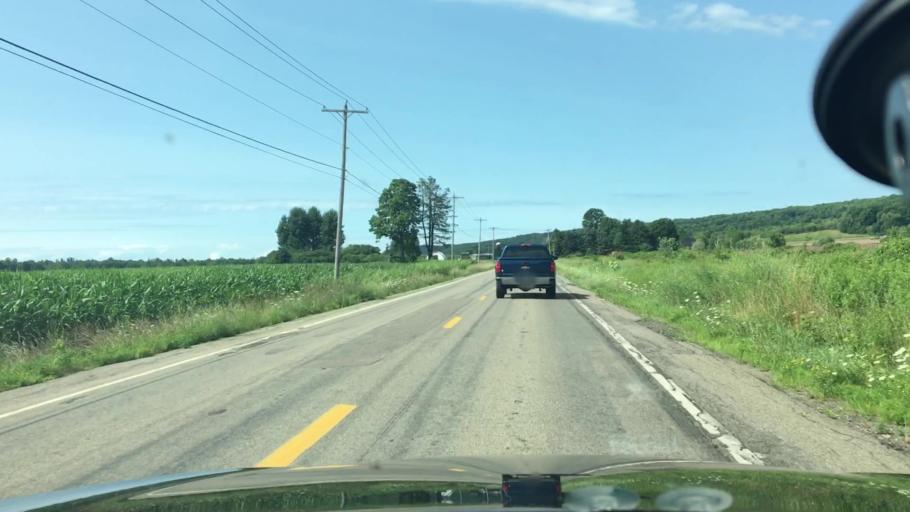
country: US
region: New York
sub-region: Chautauqua County
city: Brocton
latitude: 42.2962
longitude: -79.3531
